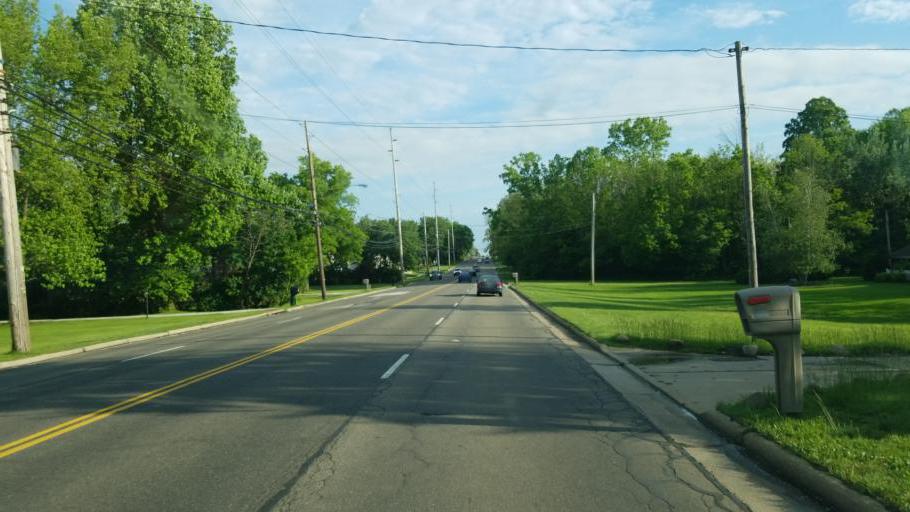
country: US
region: Ohio
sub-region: Summit County
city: Stow
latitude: 41.1811
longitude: -81.4405
